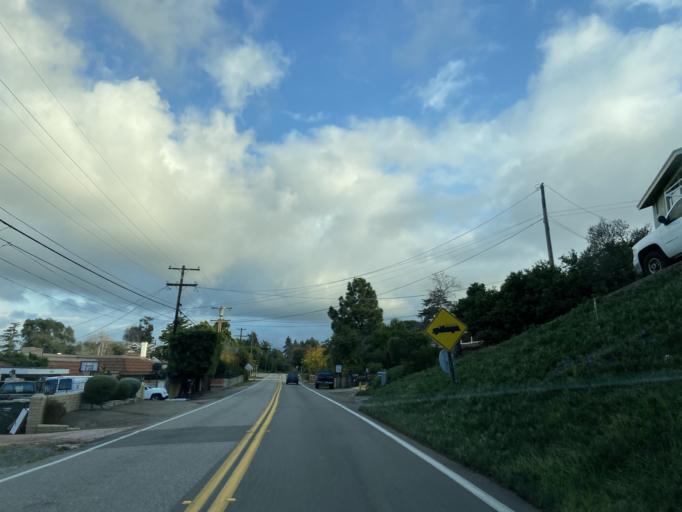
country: US
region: California
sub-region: San Diego County
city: Casa de Oro-Mount Helix
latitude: 32.7716
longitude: -116.9778
